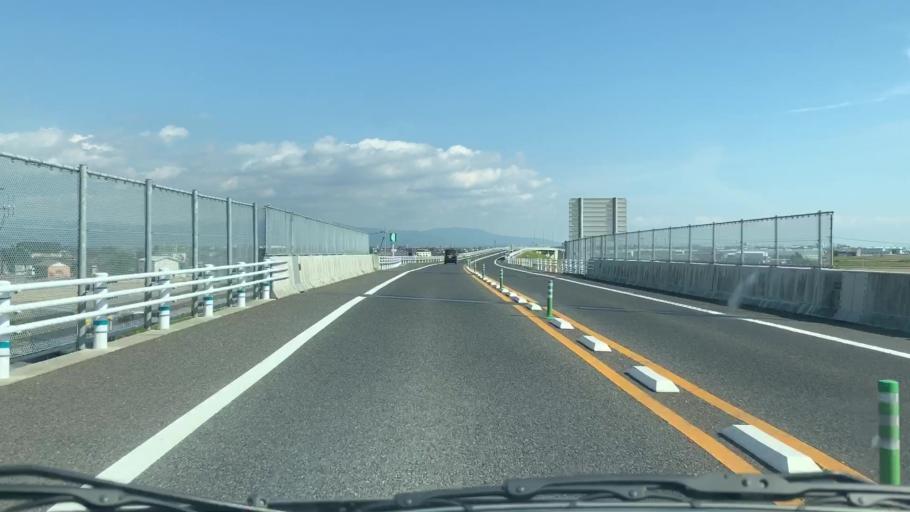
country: JP
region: Saga Prefecture
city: Saga-shi
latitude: 33.2267
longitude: 130.2189
